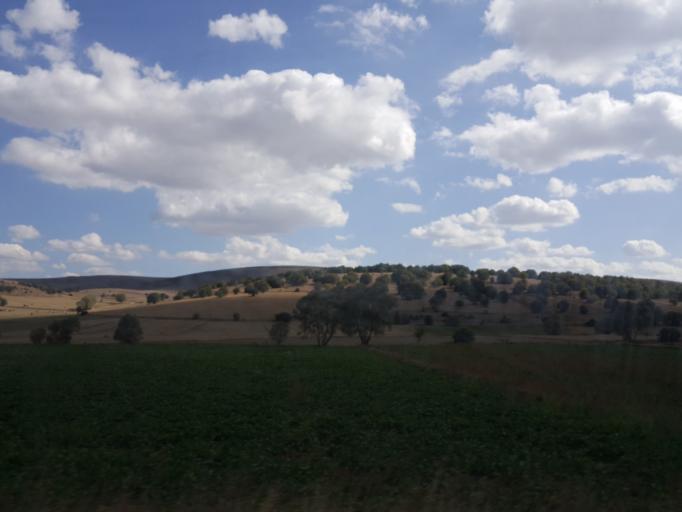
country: TR
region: Tokat
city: Camlibel
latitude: 40.1638
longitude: 36.4221
